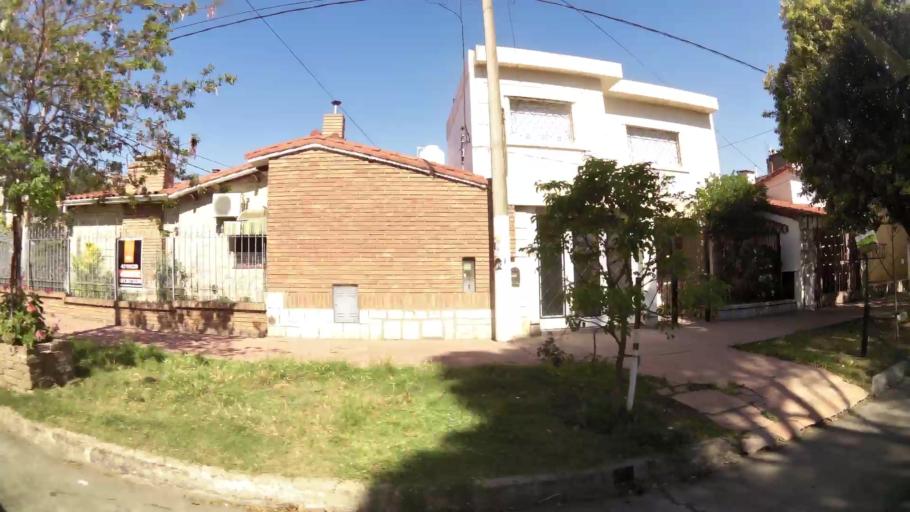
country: AR
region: Cordoba
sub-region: Departamento de Capital
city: Cordoba
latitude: -31.4176
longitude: -64.1622
